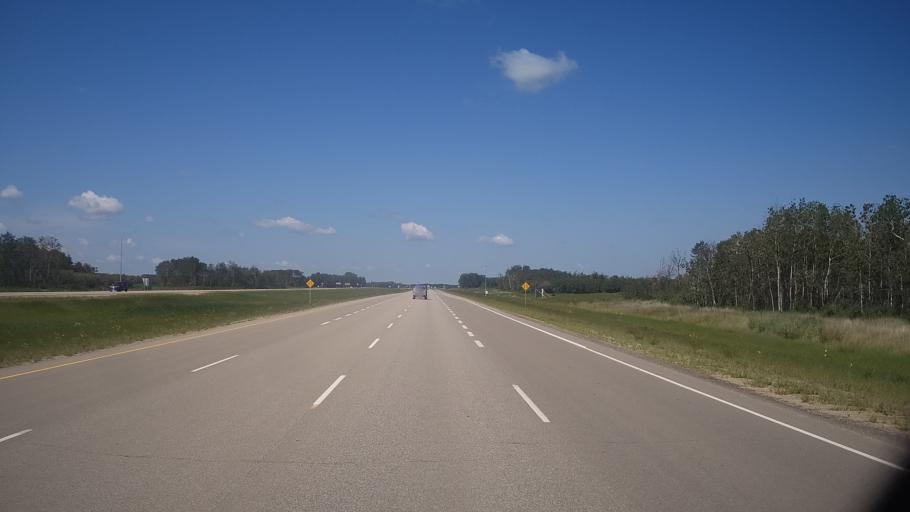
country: CA
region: Saskatchewan
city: Saskatoon
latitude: 52.0123
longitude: -106.3910
